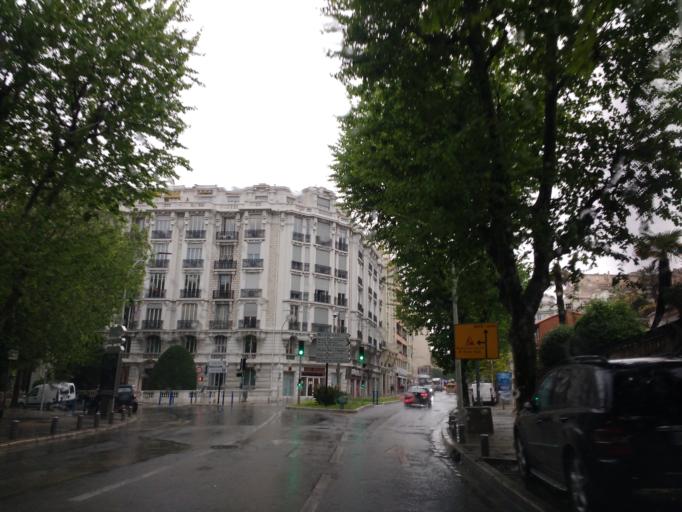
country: FR
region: Provence-Alpes-Cote d'Azur
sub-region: Departement des Alpes-Maritimes
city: Nice
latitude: 43.7042
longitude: 7.2741
